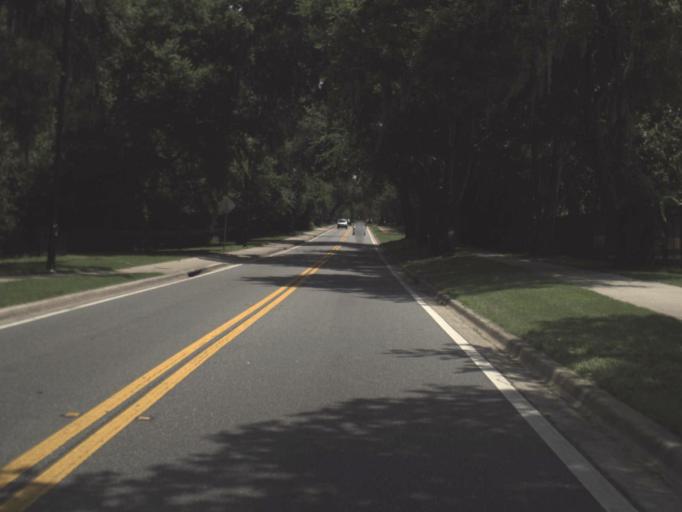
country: US
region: Florida
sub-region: Alachua County
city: Gainesville
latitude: 29.6506
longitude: -82.3550
